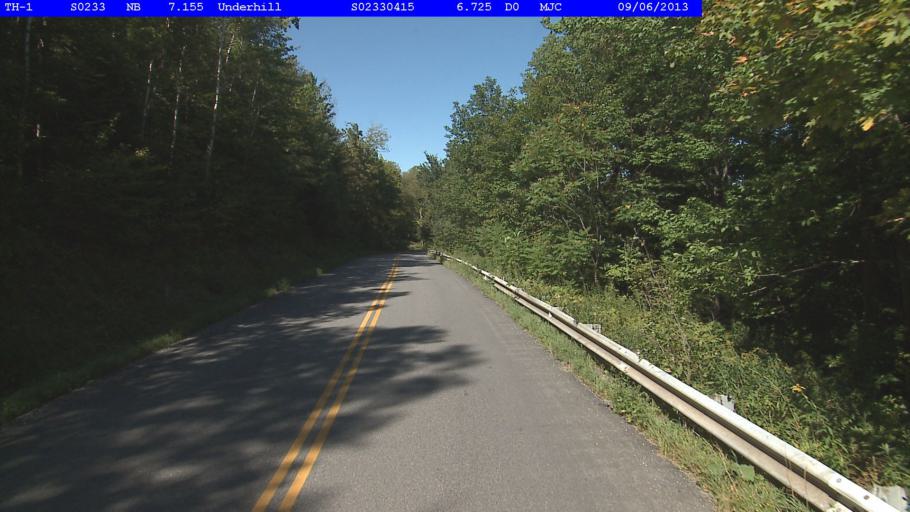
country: US
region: Vermont
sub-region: Chittenden County
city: Jericho
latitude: 44.5617
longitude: -72.8657
